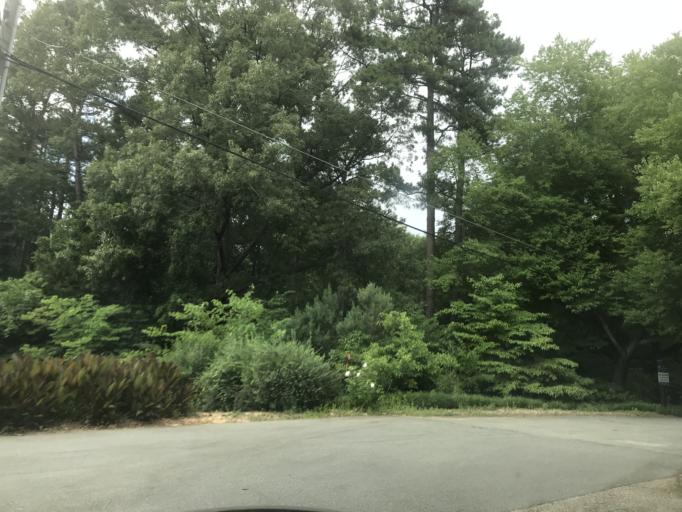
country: US
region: North Carolina
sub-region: Wake County
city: West Raleigh
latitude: 35.8271
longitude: -78.6401
